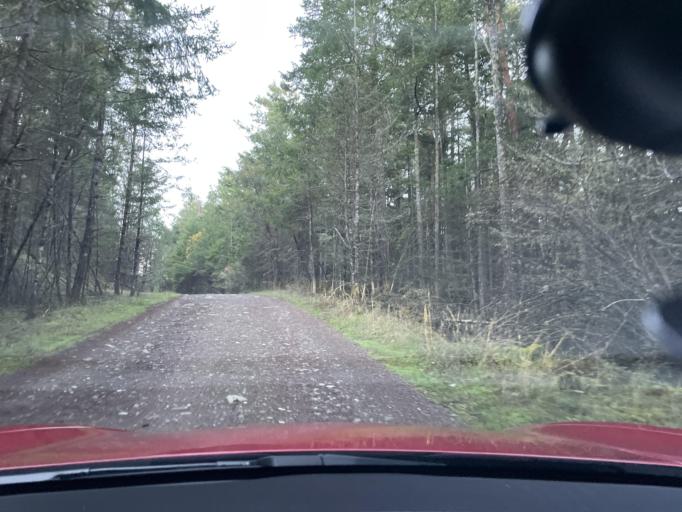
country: US
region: Washington
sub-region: San Juan County
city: Friday Harbor
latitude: 48.6170
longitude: -123.1407
